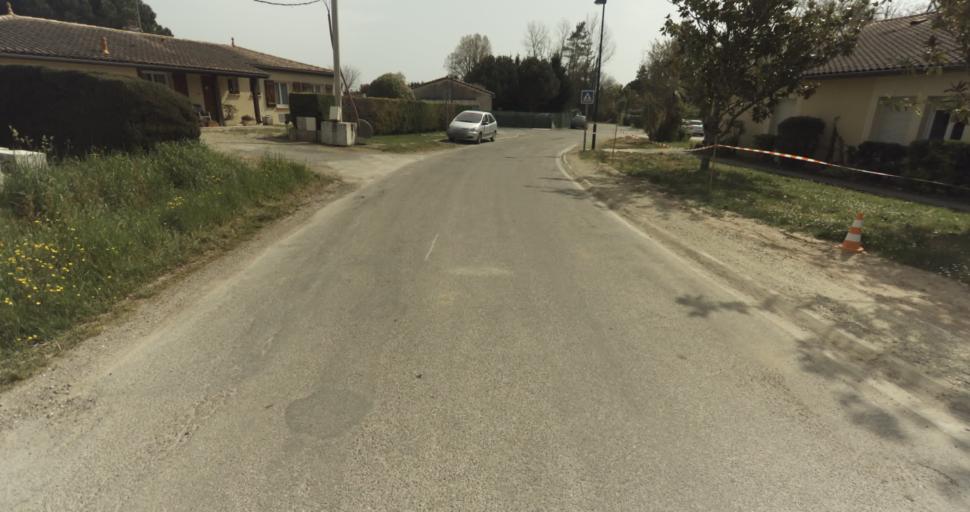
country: FR
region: Midi-Pyrenees
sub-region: Departement du Tarn-et-Garonne
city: Moissac
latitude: 44.1171
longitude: 1.1091
